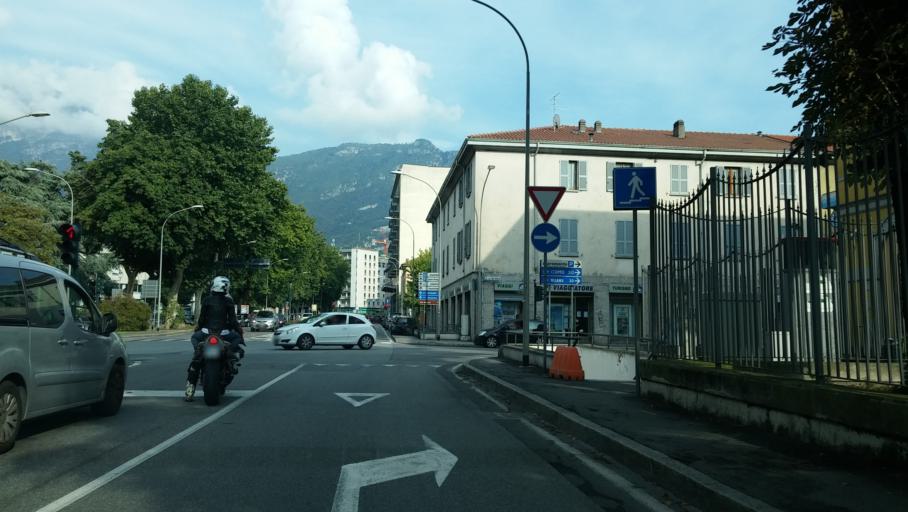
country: IT
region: Lombardy
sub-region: Provincia di Lecco
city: Lecco
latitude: 45.8525
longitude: 9.3884
